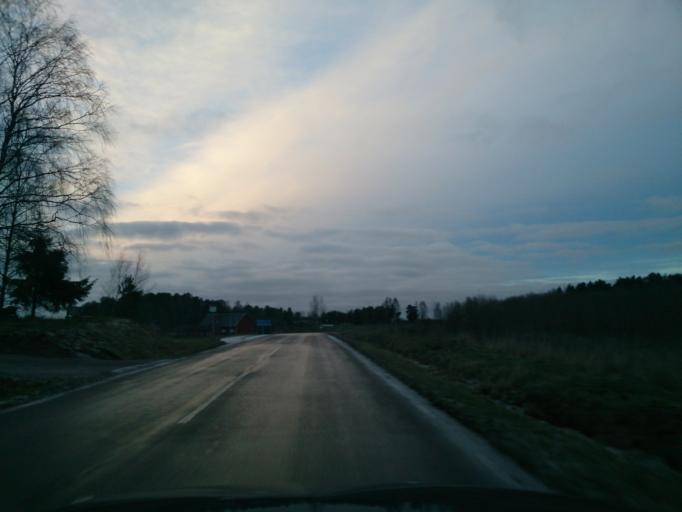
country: SE
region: OEstergoetland
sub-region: Norrkopings Kommun
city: Kimstad
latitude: 58.3953
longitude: 15.9650
